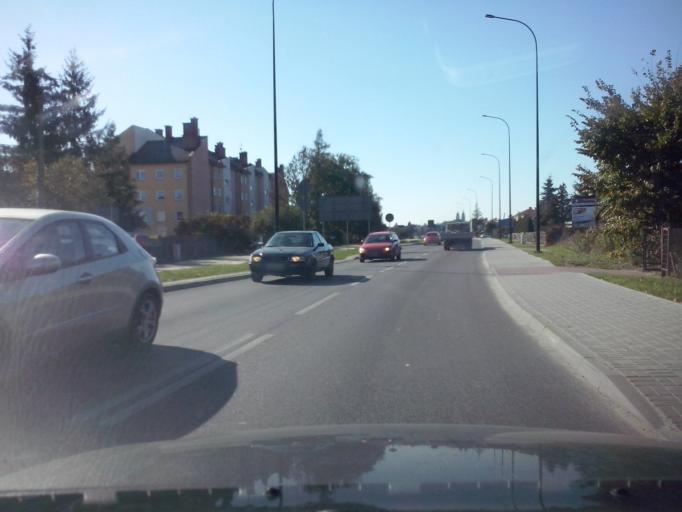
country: PL
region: Lublin Voivodeship
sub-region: Powiat bilgorajski
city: Bilgoraj
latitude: 50.5485
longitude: 22.7386
